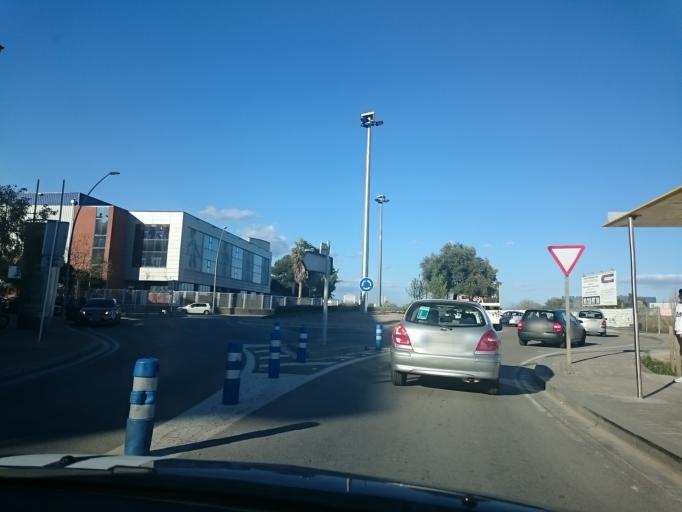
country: ES
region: Catalonia
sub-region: Provincia de Barcelona
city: Castelldefels
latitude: 41.2875
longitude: 1.9889
